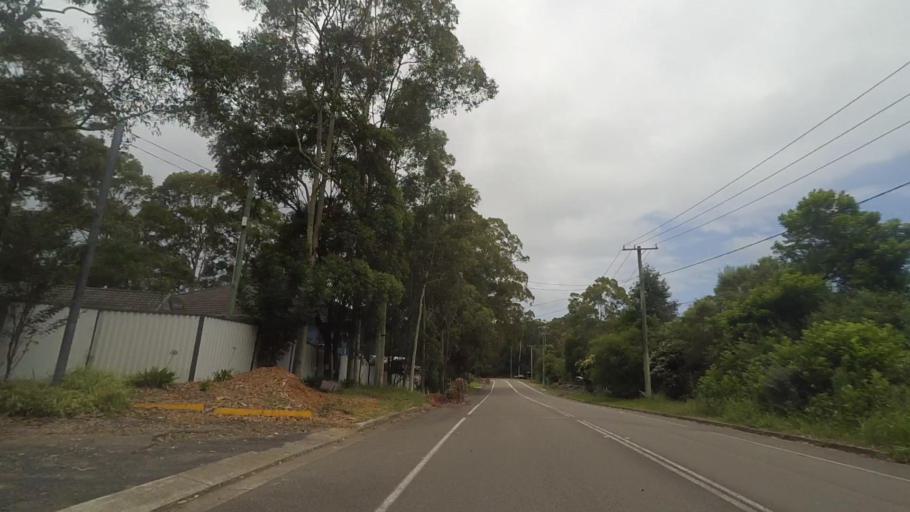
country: AU
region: New South Wales
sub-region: Wyong Shire
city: Chittaway Bay
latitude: -33.3402
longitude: 151.4199
